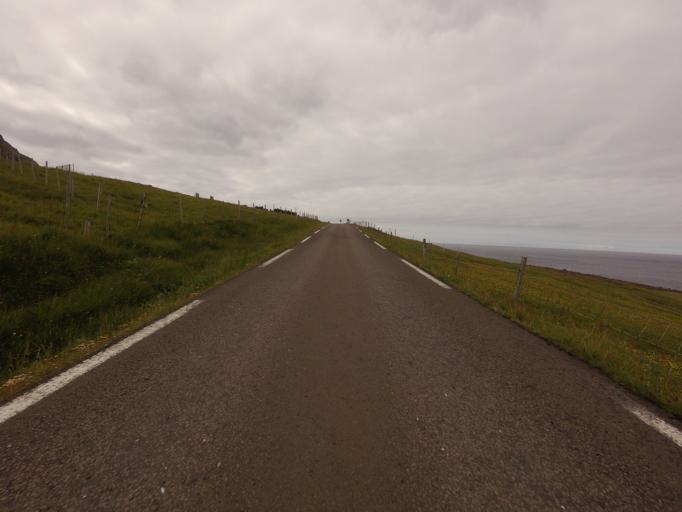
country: FO
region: Suduroy
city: Tvoroyri
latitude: 61.5195
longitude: -6.8883
